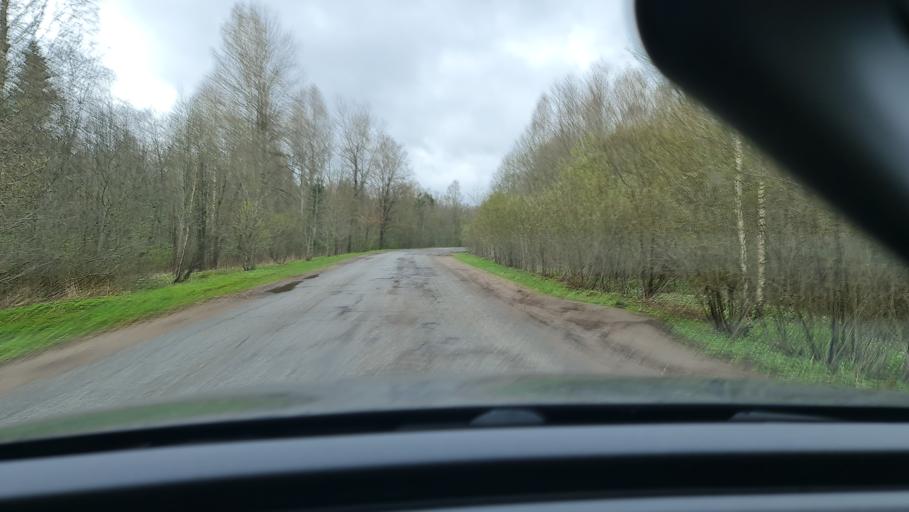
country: RU
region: Novgorod
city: Marevo
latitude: 57.2691
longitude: 32.0826
